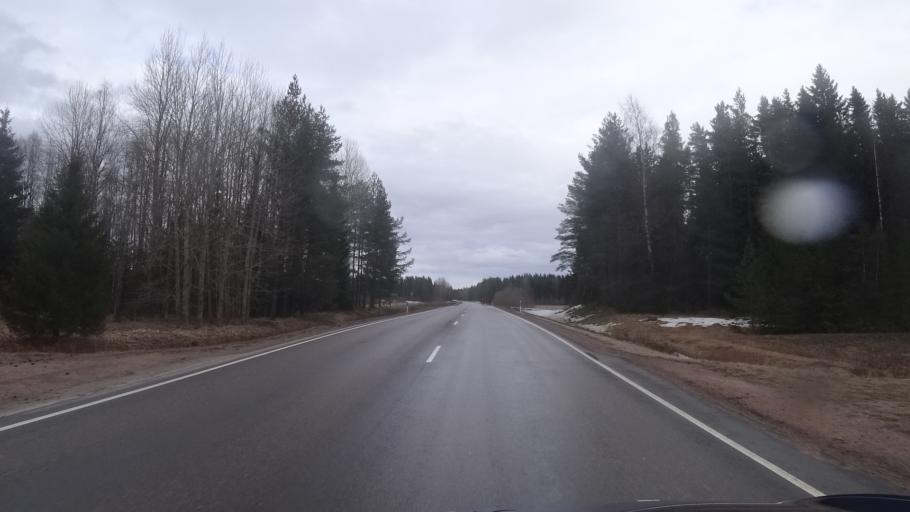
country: FI
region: Kymenlaakso
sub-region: Kouvola
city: Elimaeki
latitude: 60.6898
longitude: 26.6054
